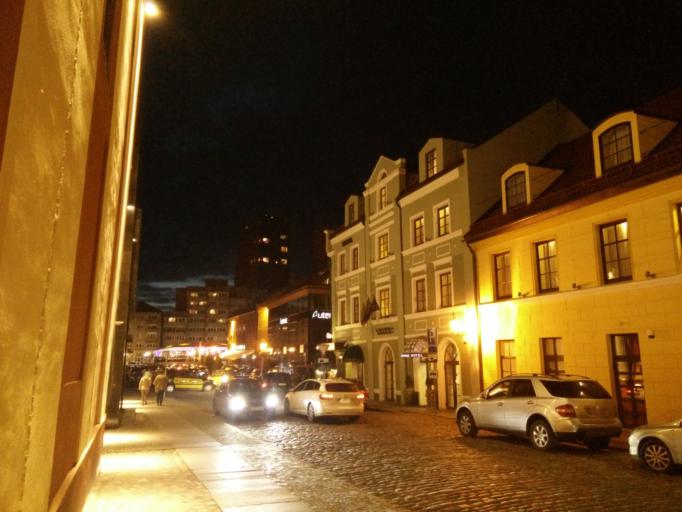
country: LT
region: Klaipedos apskritis
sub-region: Klaipeda
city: Klaipeda
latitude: 55.7082
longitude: 21.1315
